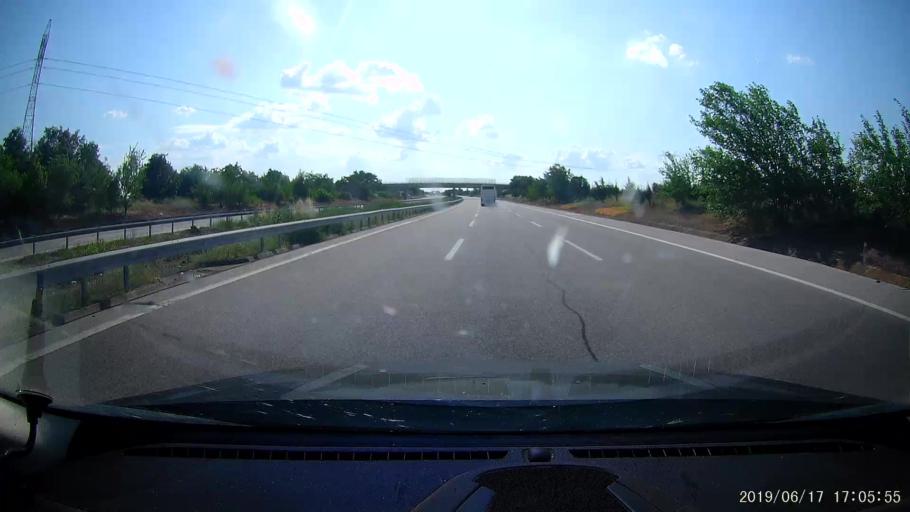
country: TR
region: Edirne
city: Edirne
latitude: 41.6622
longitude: 26.6857
